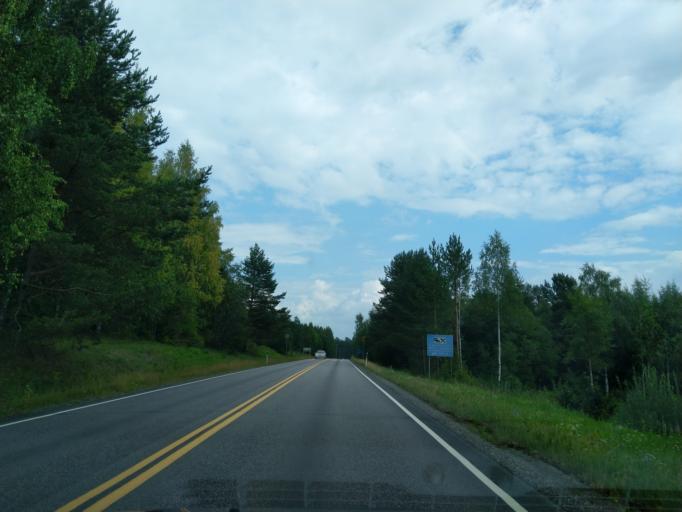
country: FI
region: South Karelia
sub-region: Imatra
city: Parikkala
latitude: 61.6037
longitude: 29.4731
